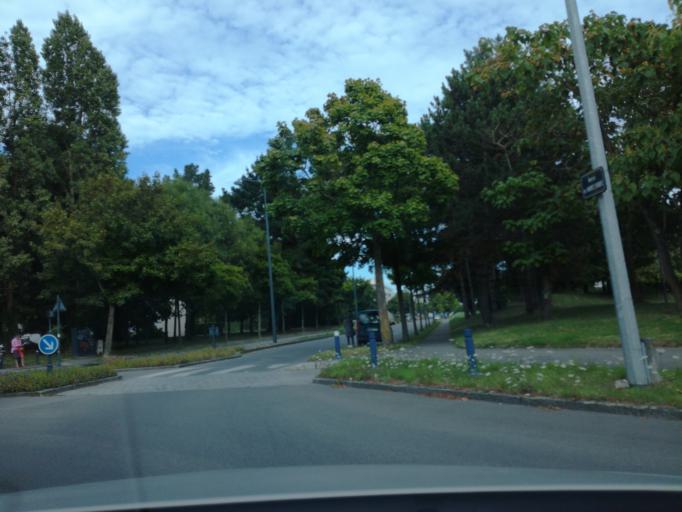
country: FR
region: Brittany
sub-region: Departement d'Ille-et-Vilaine
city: Saint-Gregoire
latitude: 48.1365
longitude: -1.6670
